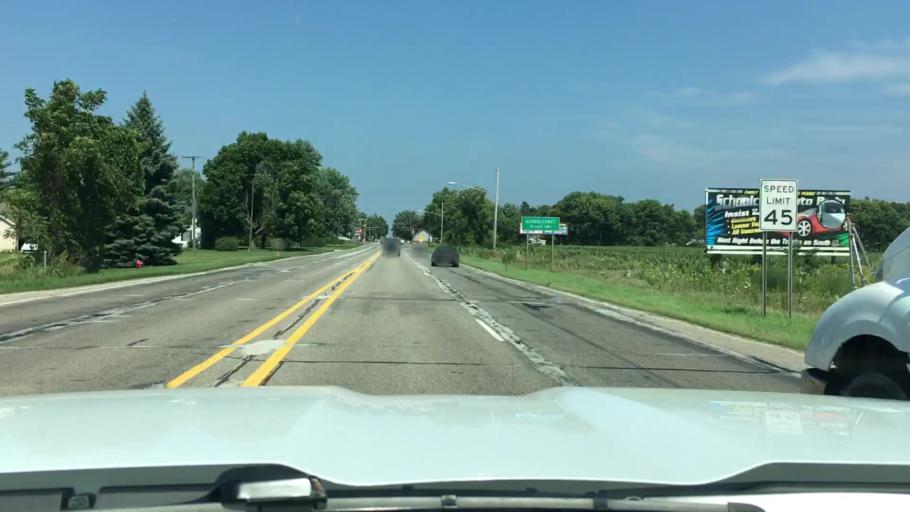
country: US
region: Michigan
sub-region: Kalamazoo County
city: Schoolcraft
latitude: 42.1064
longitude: -85.6371
